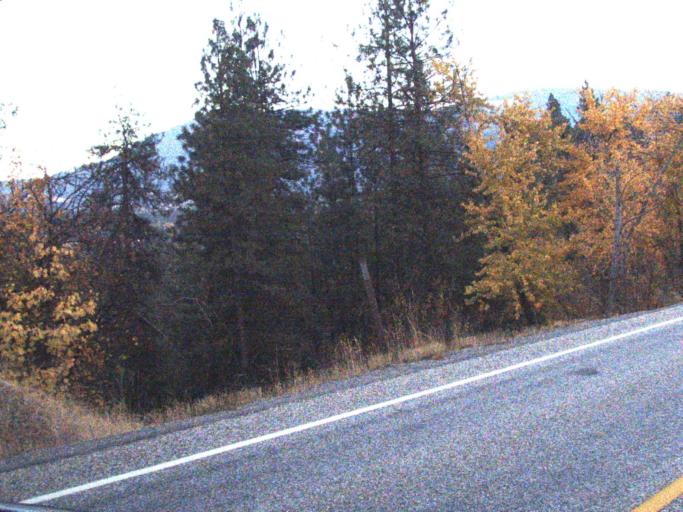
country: US
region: Washington
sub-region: Stevens County
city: Kettle Falls
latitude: 48.6140
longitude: -118.1385
